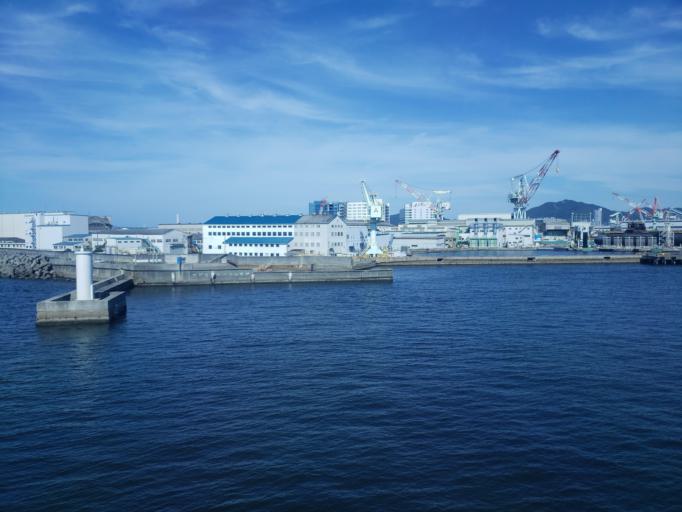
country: JP
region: Hyogo
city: Kobe
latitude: 34.6530
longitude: 135.1885
